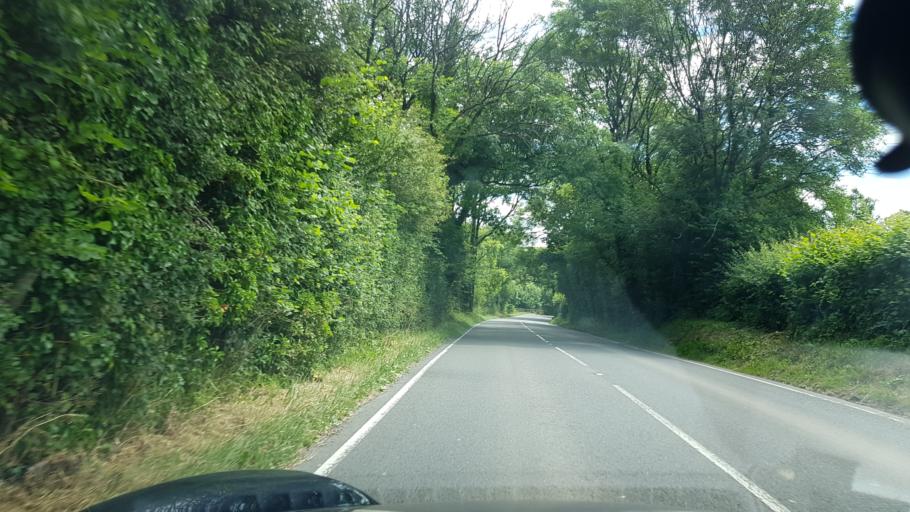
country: GB
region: Wales
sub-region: Carmarthenshire
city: Saint Clears
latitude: 51.7987
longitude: -4.4892
